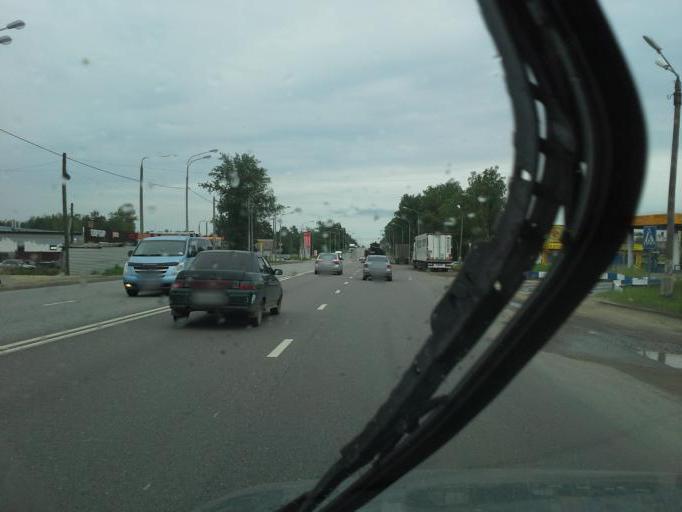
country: RU
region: Vladimir
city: Pokrov
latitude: 55.9197
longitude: 39.1977
